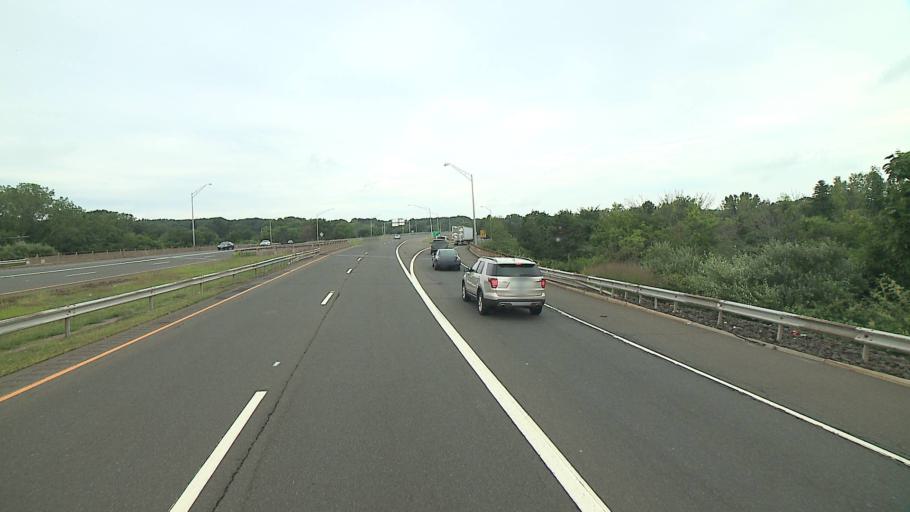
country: US
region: Connecticut
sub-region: New Haven County
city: North Haven
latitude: 41.3780
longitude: -72.8800
